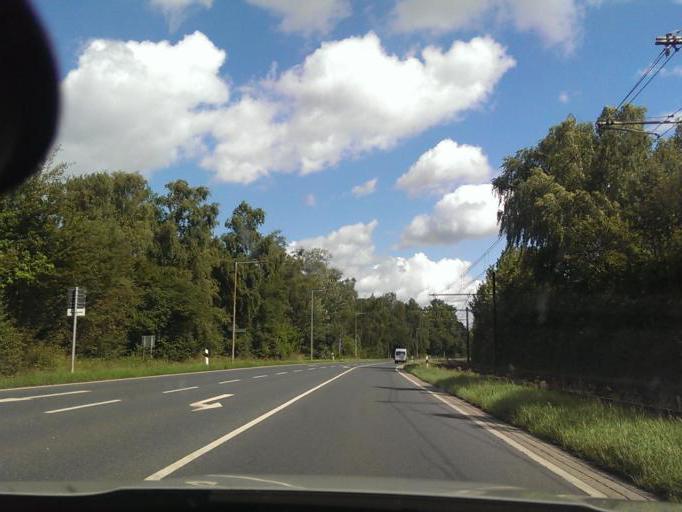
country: DE
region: Lower Saxony
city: Sarstedt
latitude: 52.2492
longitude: 9.8567
